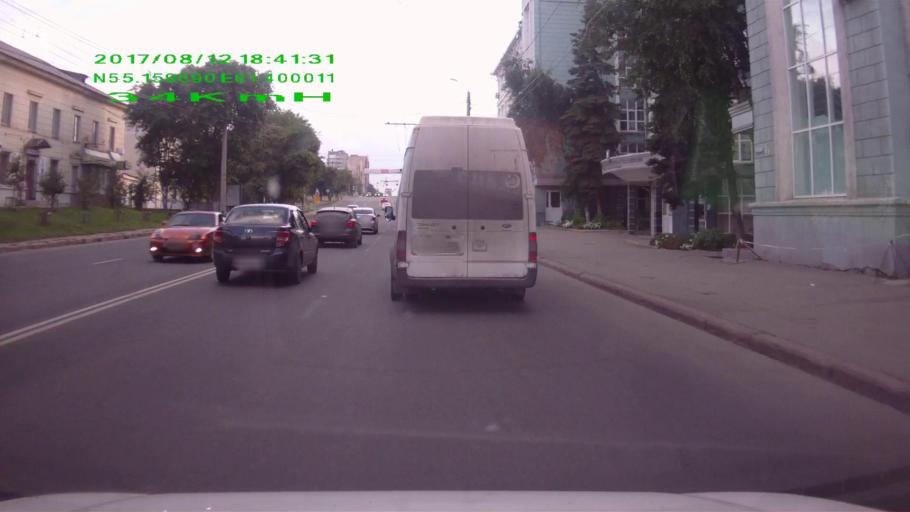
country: RU
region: Chelyabinsk
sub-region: Gorod Chelyabinsk
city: Chelyabinsk
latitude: 55.1564
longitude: 61.3957
